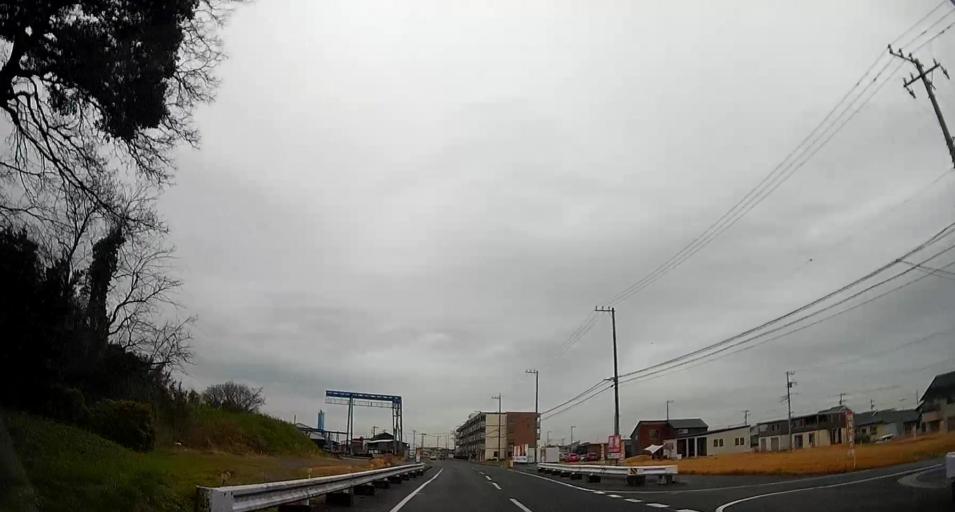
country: JP
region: Chiba
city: Kisarazu
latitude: 35.4278
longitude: 139.9394
